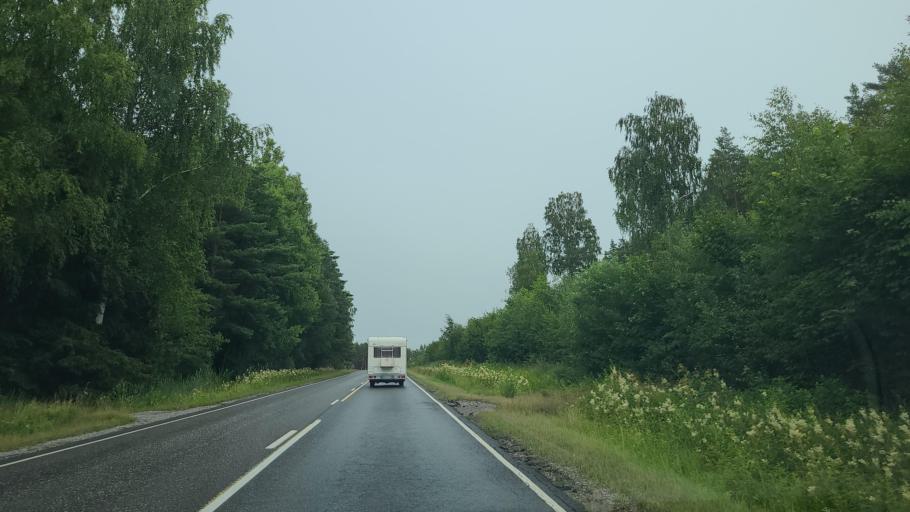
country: FI
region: Varsinais-Suomi
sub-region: Turku
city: Sauvo
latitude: 60.3172
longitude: 22.7011
